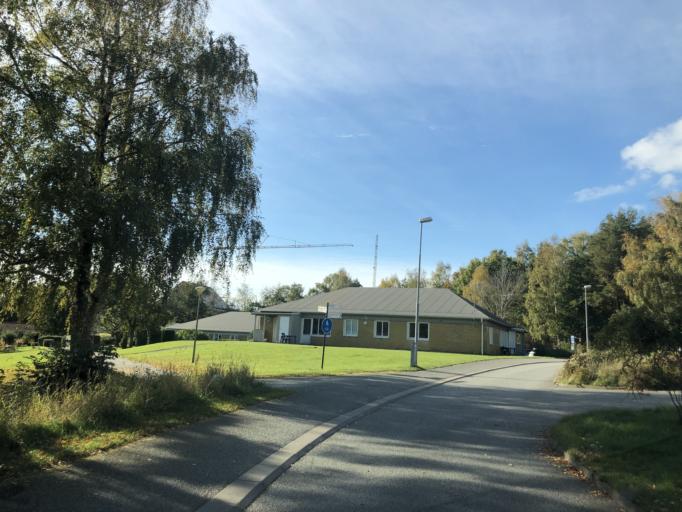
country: SE
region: Vaestra Goetaland
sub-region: Goteborg
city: Billdal
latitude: 57.6297
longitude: 11.9289
